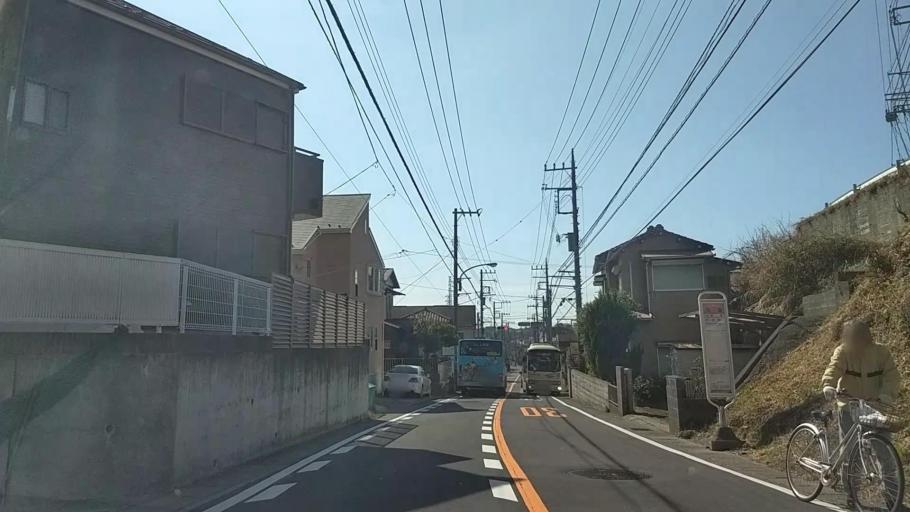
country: JP
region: Kanagawa
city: Kamakura
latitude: 35.3671
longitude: 139.5404
